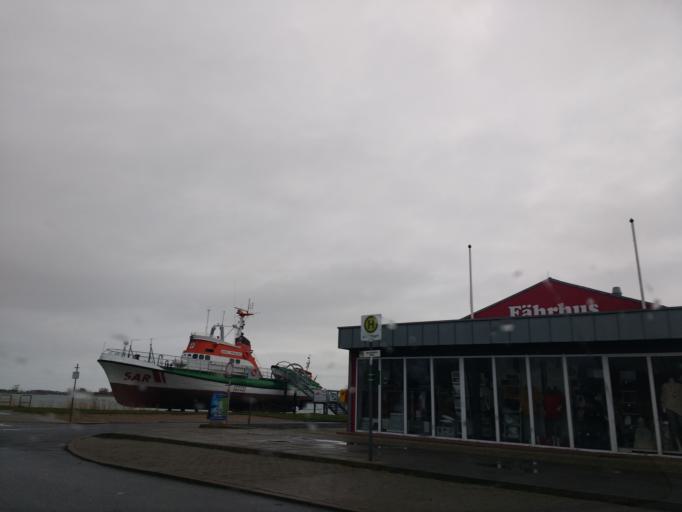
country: DE
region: Schleswig-Holstein
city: Burg auf Fehmarn
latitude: 54.4199
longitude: 11.1923
